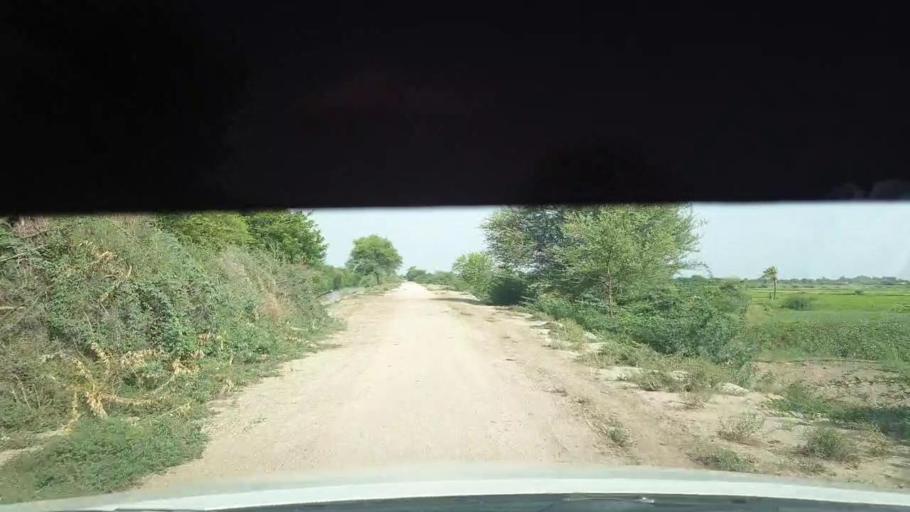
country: PK
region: Sindh
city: Kadhan
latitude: 24.5181
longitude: 69.0063
